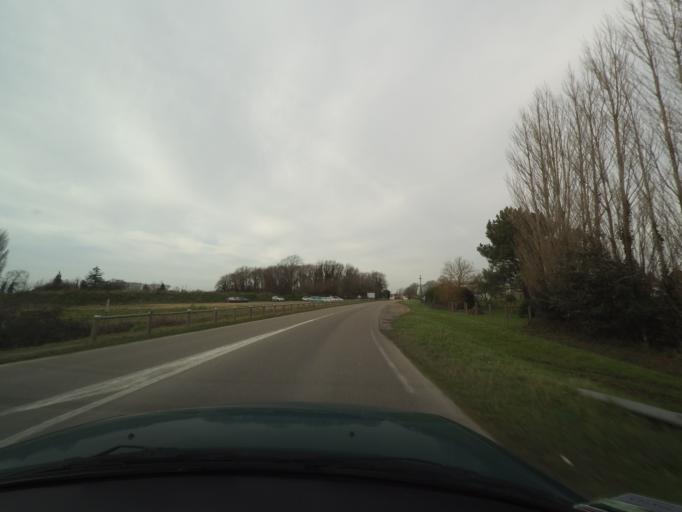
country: FR
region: Pays de la Loire
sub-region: Departement de la Loire-Atlantique
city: Arthon-en-Retz
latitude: 47.1180
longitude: -1.9517
